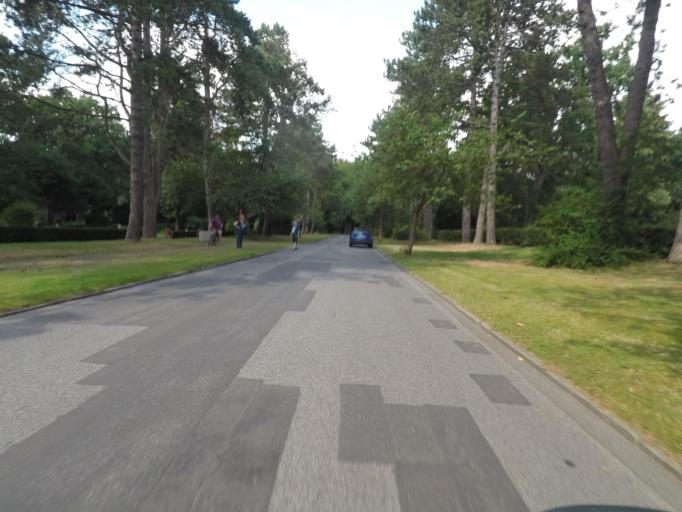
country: DE
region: Hamburg
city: Wellingsbuettel
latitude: 53.6284
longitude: 10.0732
